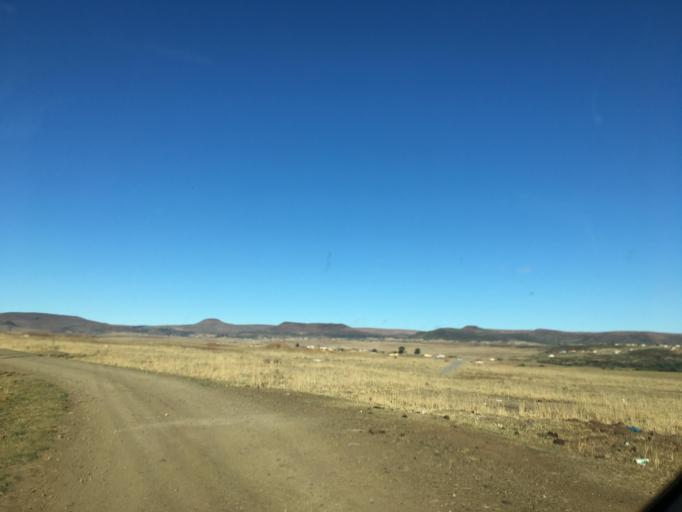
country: ZA
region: Eastern Cape
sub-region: Chris Hani District Municipality
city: Cala
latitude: -31.5378
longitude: 27.6799
